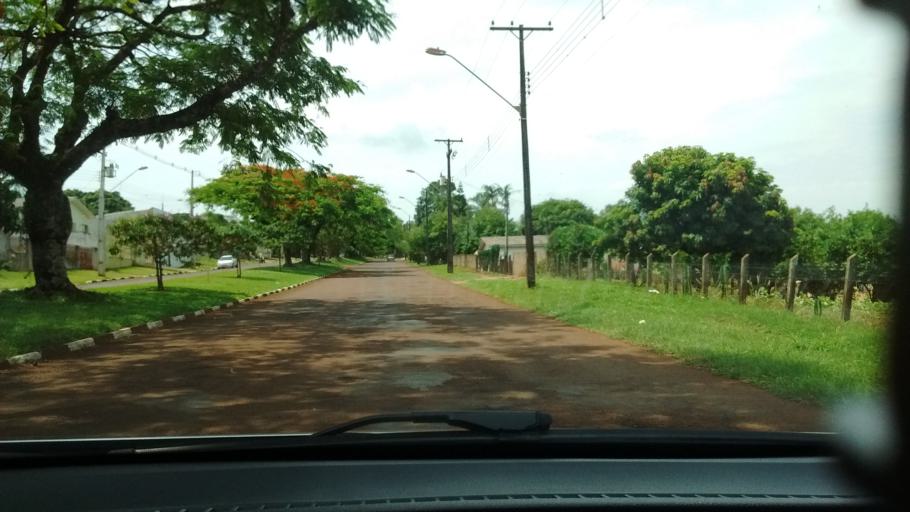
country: BR
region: Parana
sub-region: Corbelia
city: Corbelia
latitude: -24.5484
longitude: -52.9816
